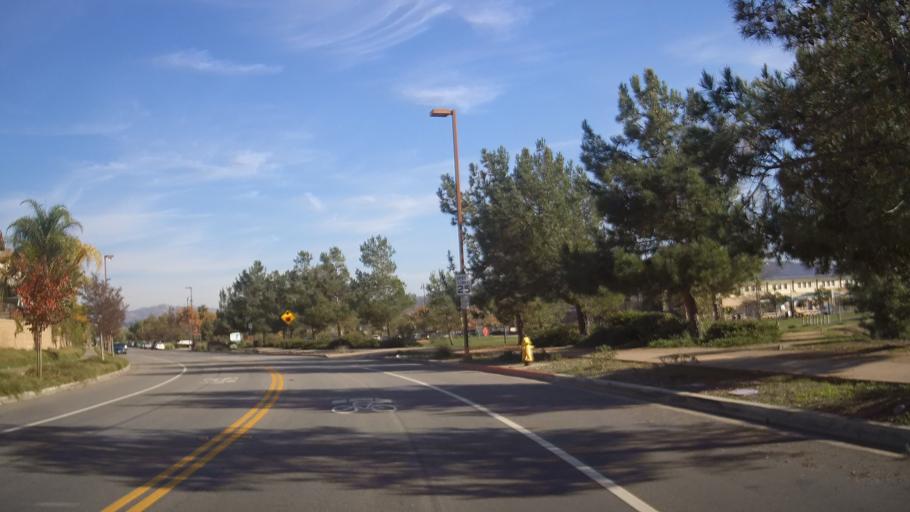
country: US
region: California
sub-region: San Diego County
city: Santee
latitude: 32.8518
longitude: -116.9790
